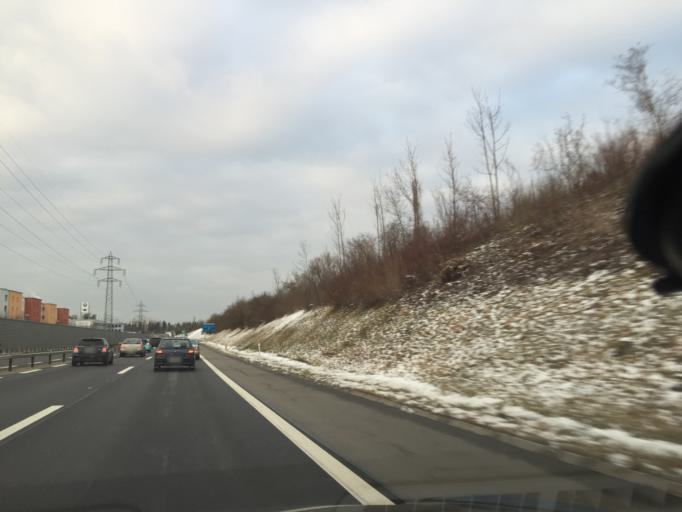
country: CH
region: Zurich
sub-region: Bezirk Horgen
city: Kilchberg / Baechler-Stocken
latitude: 47.3235
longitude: 8.5323
